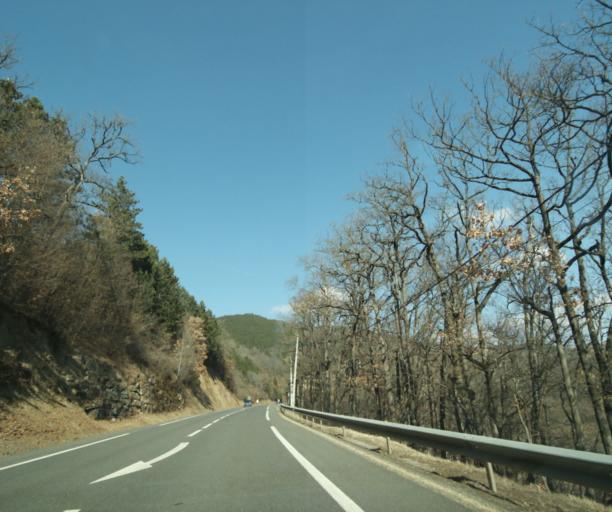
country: FR
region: Languedoc-Roussillon
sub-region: Departement de la Lozere
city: Mende
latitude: 44.5324
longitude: 3.5260
